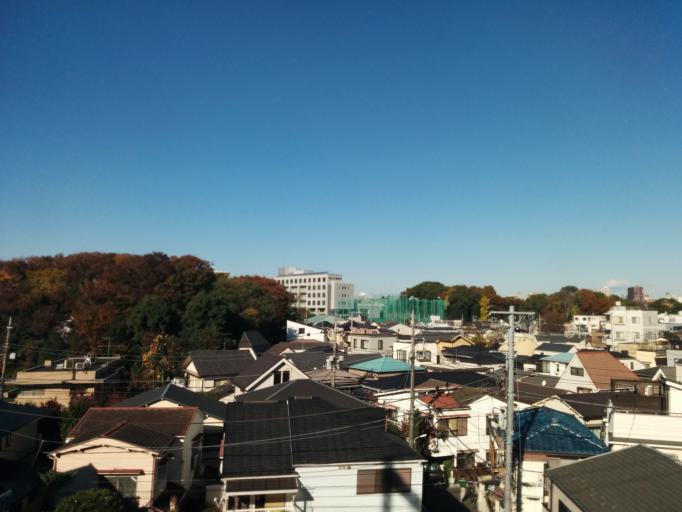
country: JP
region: Kanagawa
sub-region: Kawasaki-shi
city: Kawasaki
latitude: 35.6075
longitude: 139.7244
